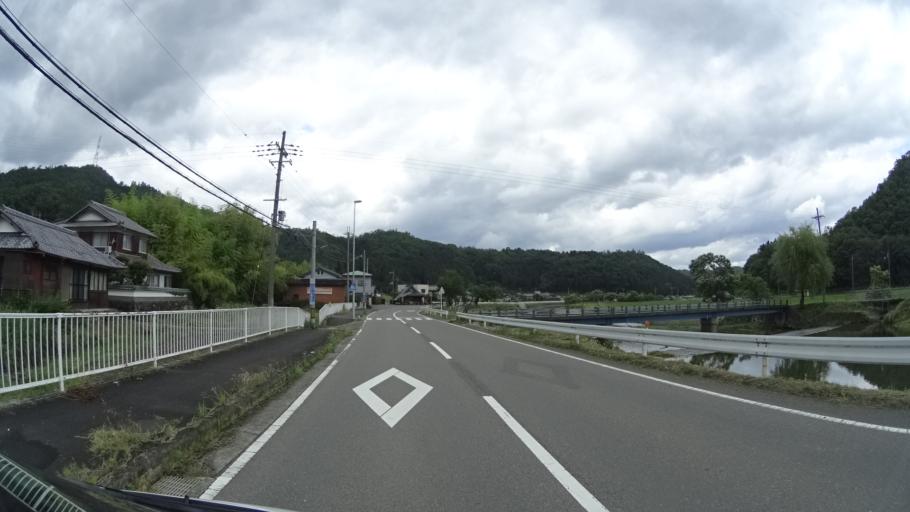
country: JP
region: Kyoto
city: Kameoka
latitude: 35.1019
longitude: 135.4350
